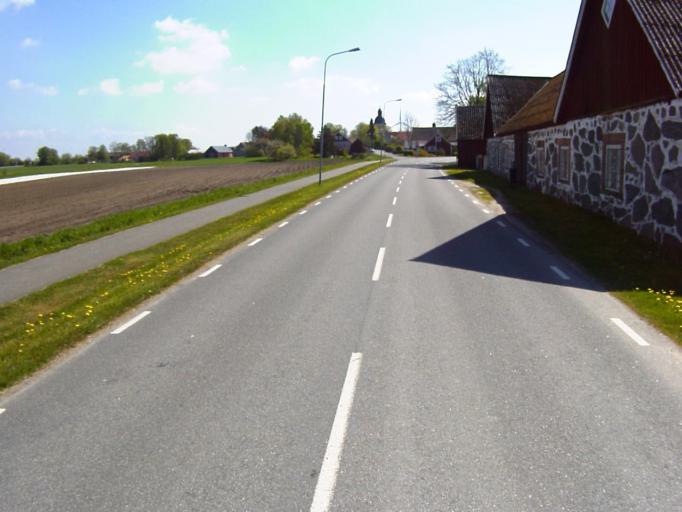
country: SE
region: Skane
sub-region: Kristianstads Kommun
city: Fjalkinge
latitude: 56.0106
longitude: 14.2415
